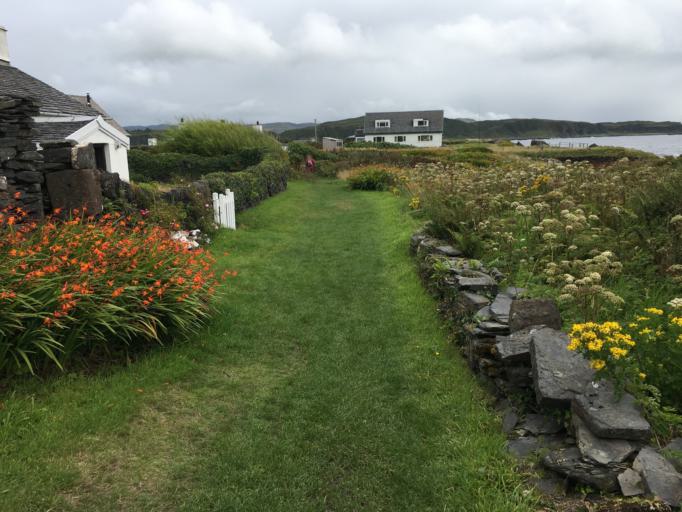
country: GB
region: Scotland
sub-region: Argyll and Bute
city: Isle Of Mull
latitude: 56.2912
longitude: -5.6575
